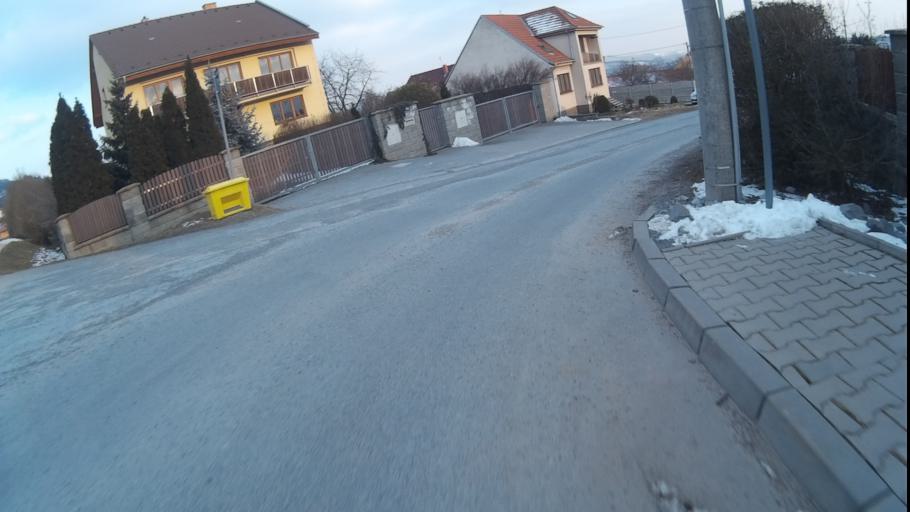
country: CZ
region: South Moravian
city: Vinicne Sumice
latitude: 49.2134
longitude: 16.8164
